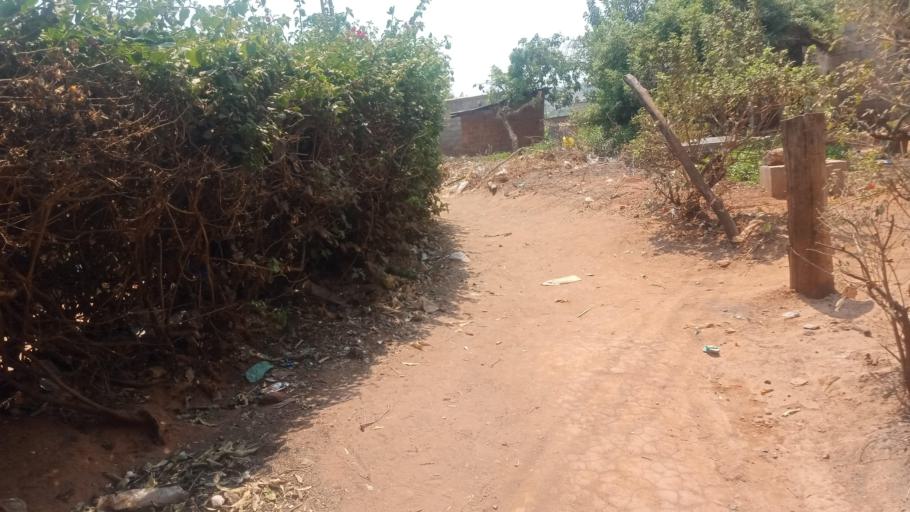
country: ZM
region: Lusaka
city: Lusaka
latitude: -15.4459
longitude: 28.3845
